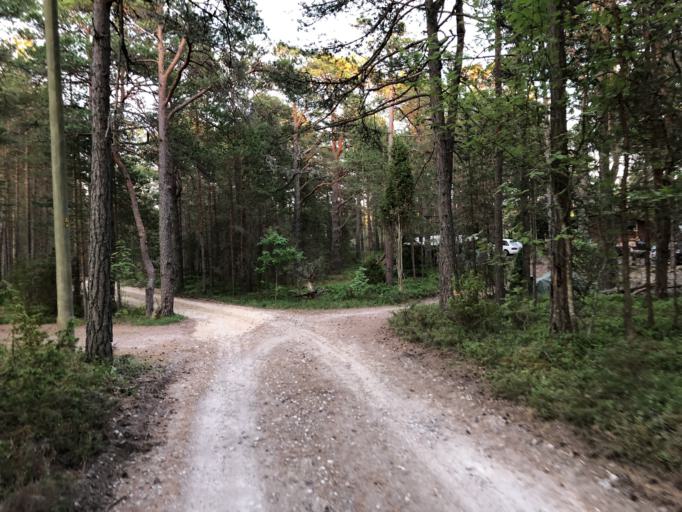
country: EE
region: Harju
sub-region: Paldiski linn
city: Paldiski
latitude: 59.3909
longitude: 24.2281
